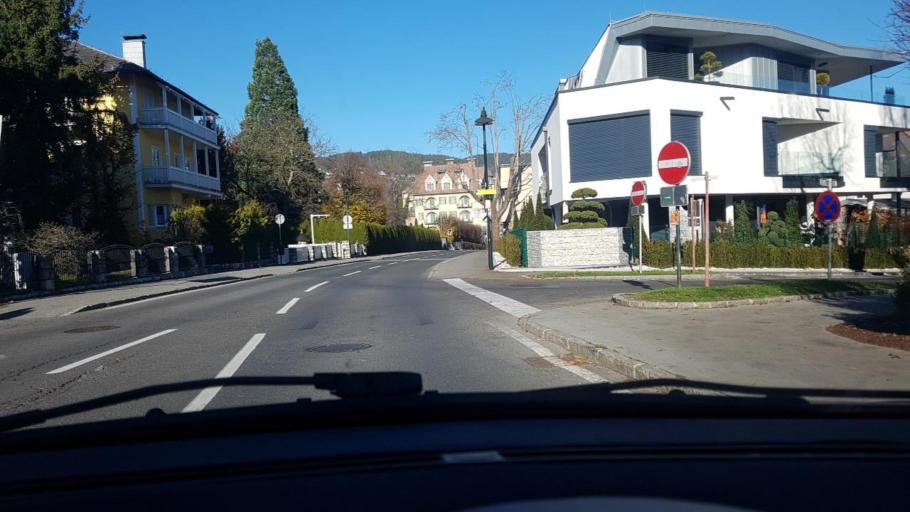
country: AT
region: Carinthia
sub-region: Politischer Bezirk Villach Land
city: Velden am Woerthersee
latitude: 46.6119
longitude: 14.0409
